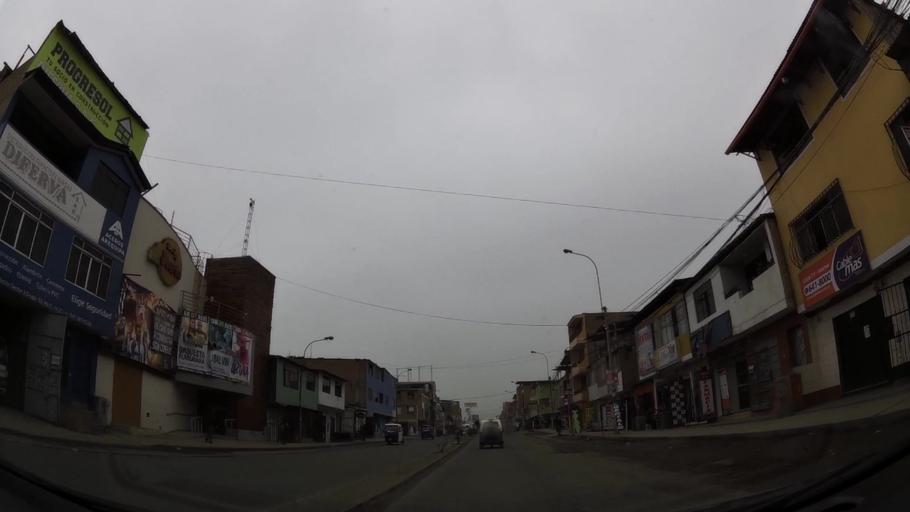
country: PE
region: Lima
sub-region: Lima
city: Surco
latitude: -12.2152
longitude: -76.9357
